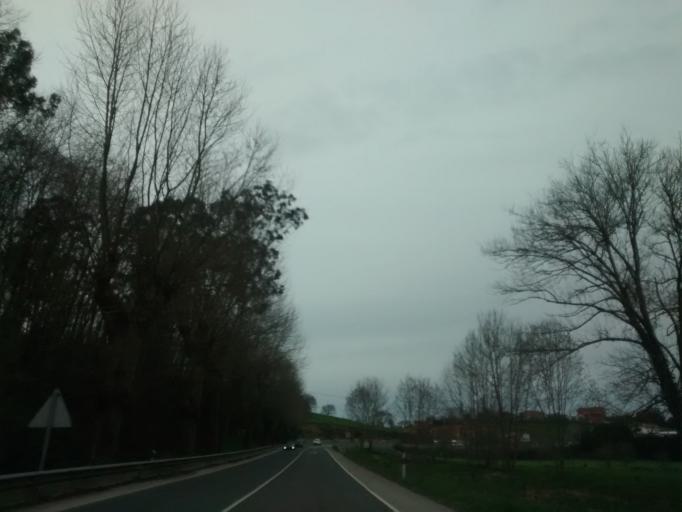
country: ES
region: Cantabria
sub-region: Provincia de Cantabria
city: Puente Viesgo
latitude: 43.3161
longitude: -3.9603
